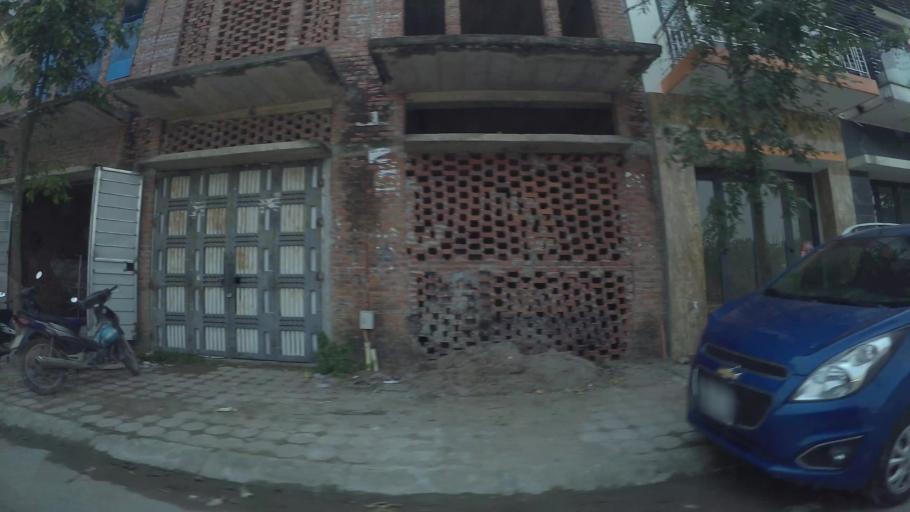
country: VN
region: Ha Noi
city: Ha Dong
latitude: 20.9714
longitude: 105.7994
